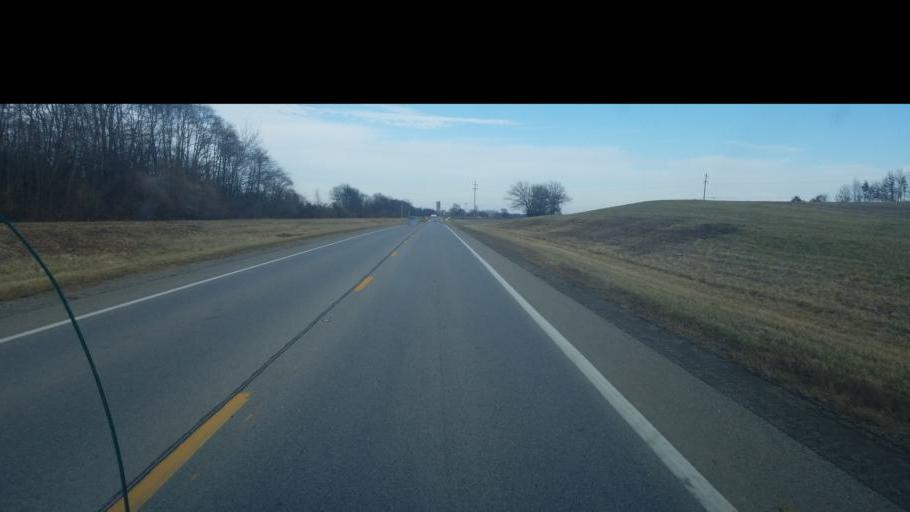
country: US
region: Illinois
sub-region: White County
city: Carmi
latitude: 38.1482
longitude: -88.0804
